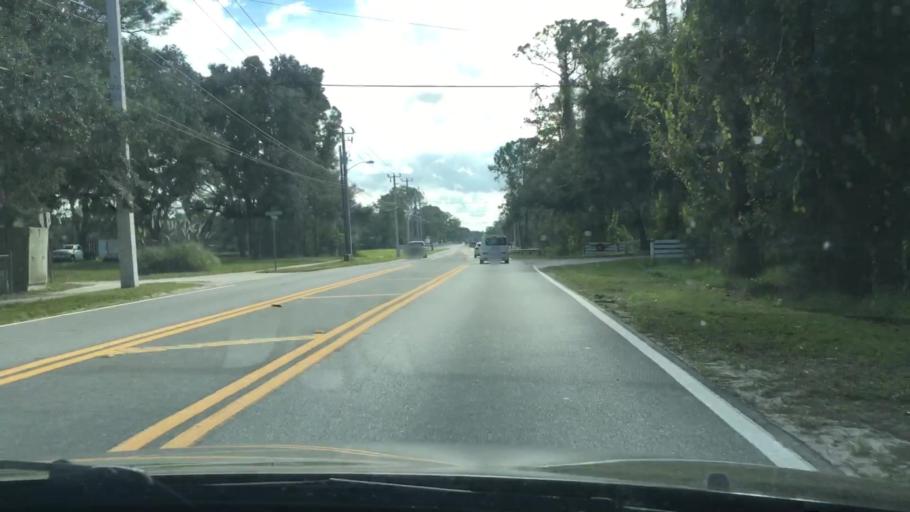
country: US
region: Florida
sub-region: Volusia County
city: Ormond Beach
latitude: 29.2673
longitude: -81.1293
